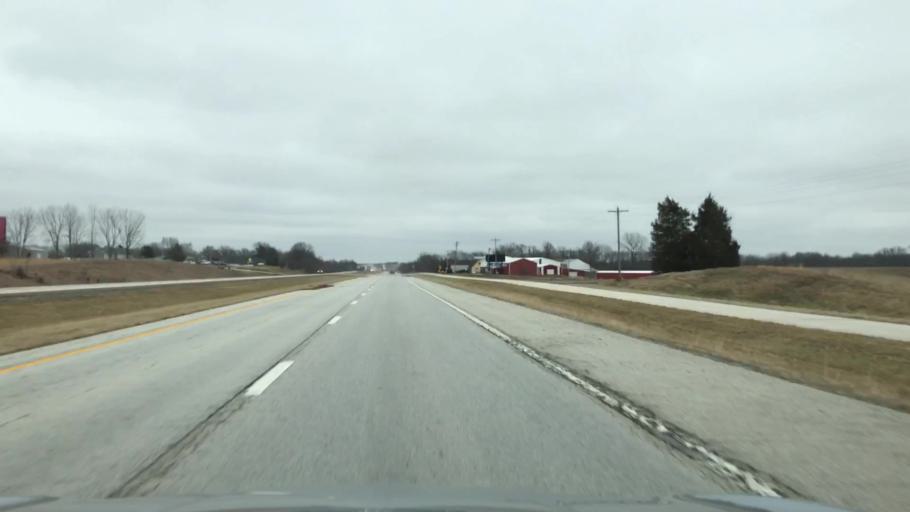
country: US
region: Missouri
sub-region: Linn County
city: Marceline
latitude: 39.7616
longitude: -92.9923
